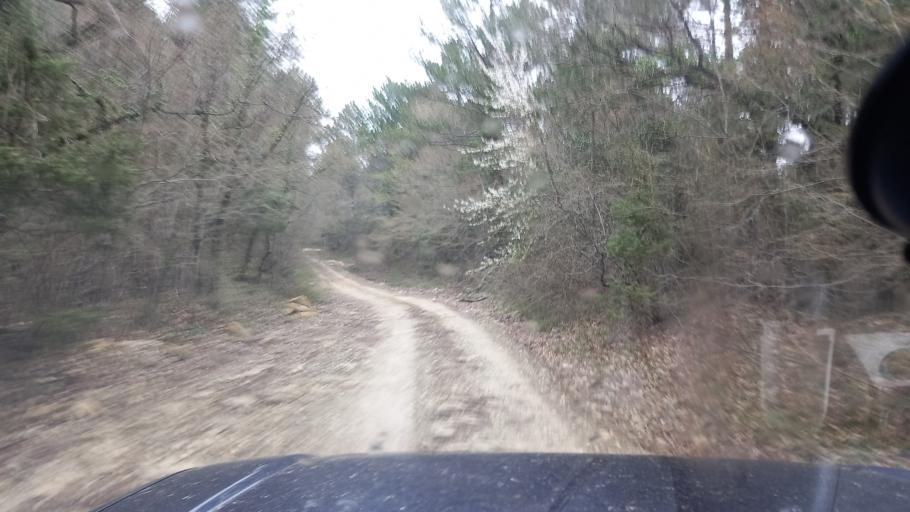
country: RU
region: Krasnodarskiy
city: Arkhipo-Osipovka
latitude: 44.3739
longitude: 38.4601
